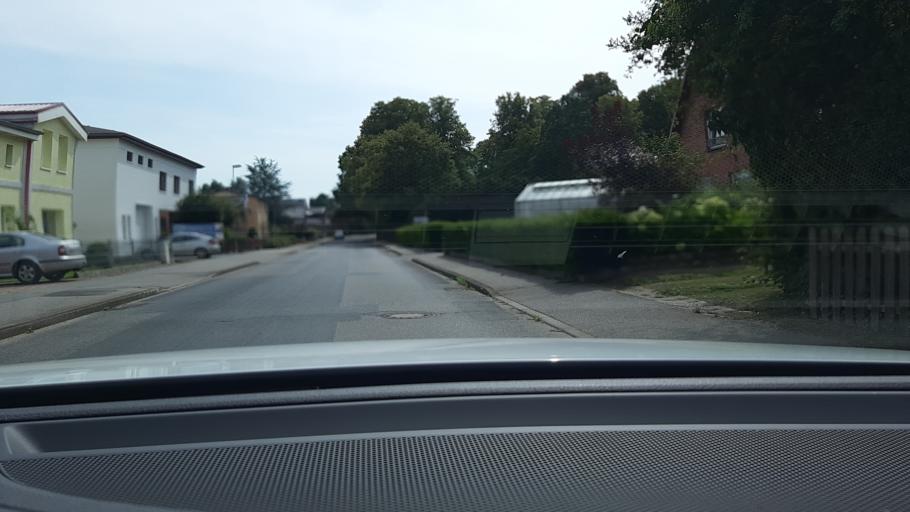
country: DE
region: Schleswig-Holstein
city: Zarpen
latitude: 53.8739
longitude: 10.5189
